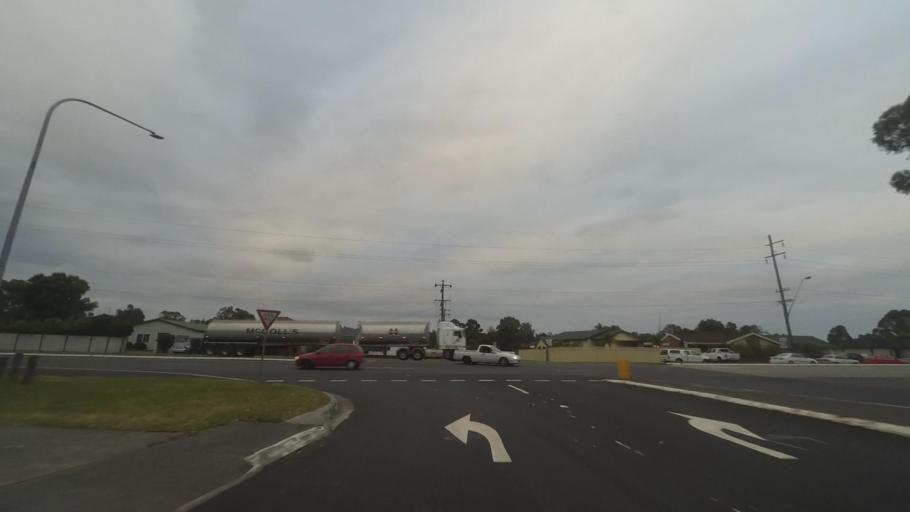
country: AU
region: New South Wales
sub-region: Shellharbour
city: Albion Park Rail
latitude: -34.5689
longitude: 150.8059
